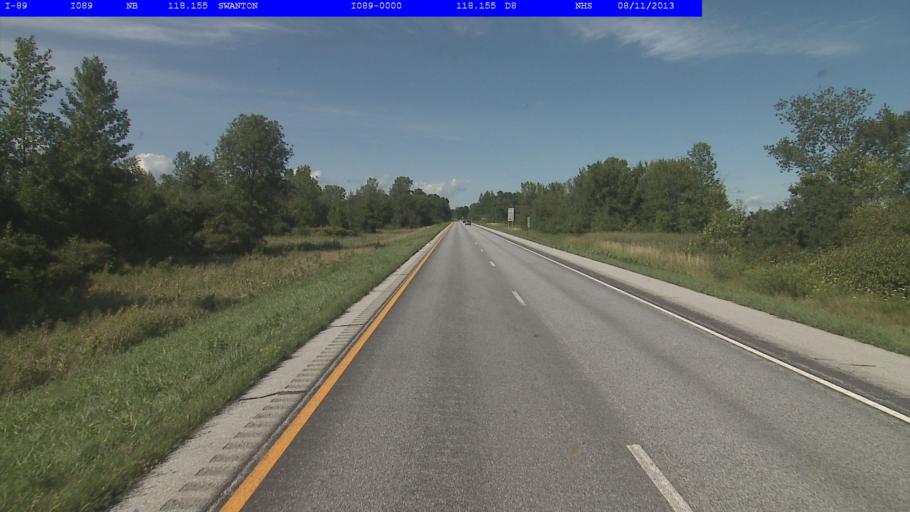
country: US
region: Vermont
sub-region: Franklin County
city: Saint Albans
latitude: 44.8506
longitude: -73.0825
